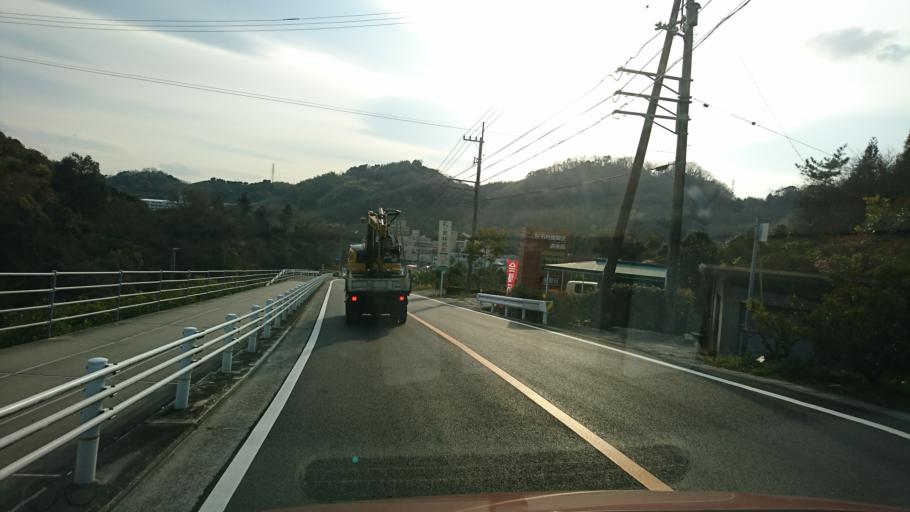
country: JP
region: Ehime
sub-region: Shikoku-chuo Shi
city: Matsuyama
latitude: 33.8674
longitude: 132.7762
